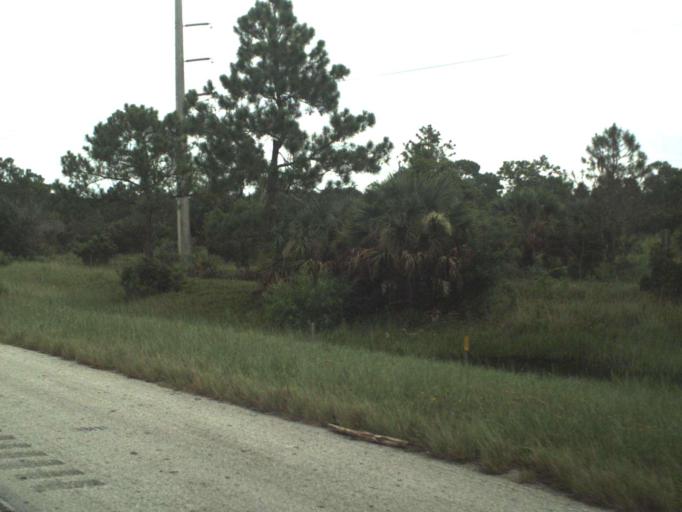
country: US
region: Florida
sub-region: Martin County
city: Palm City
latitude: 27.1002
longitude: -80.2571
